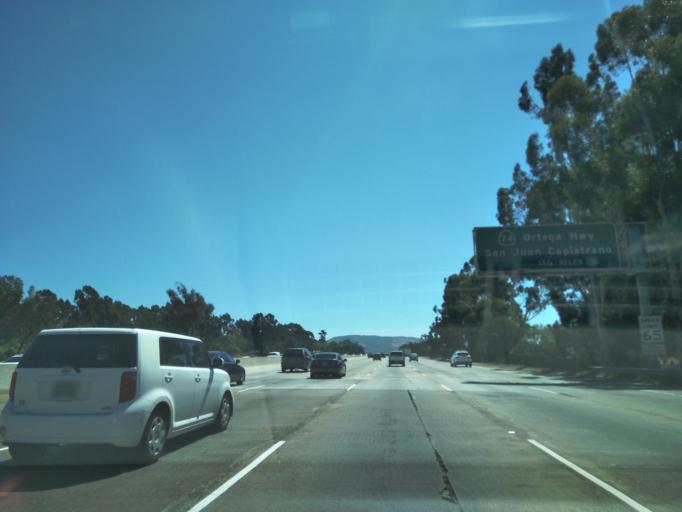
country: US
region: California
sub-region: Orange County
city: San Juan Capistrano
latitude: 33.5206
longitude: -117.6659
